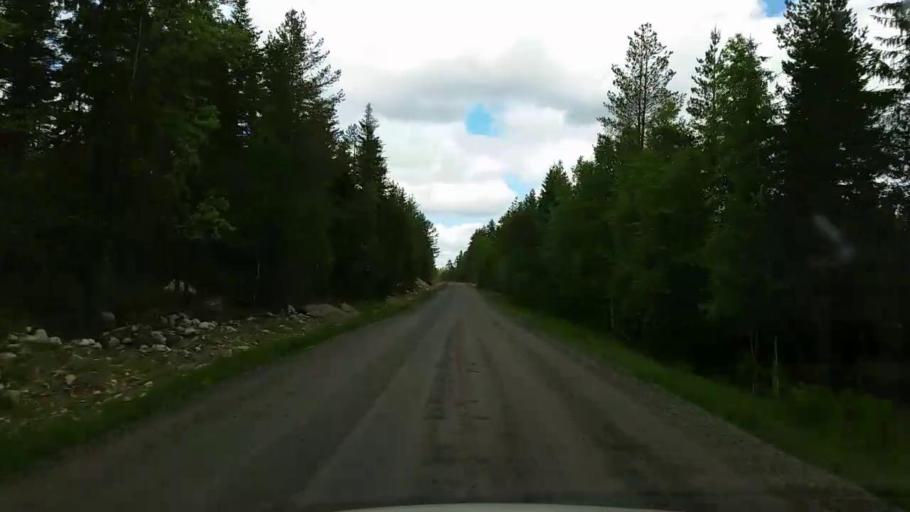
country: SE
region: Gaevleborg
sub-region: Bollnas Kommun
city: Vittsjo
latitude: 61.1633
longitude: 16.1563
